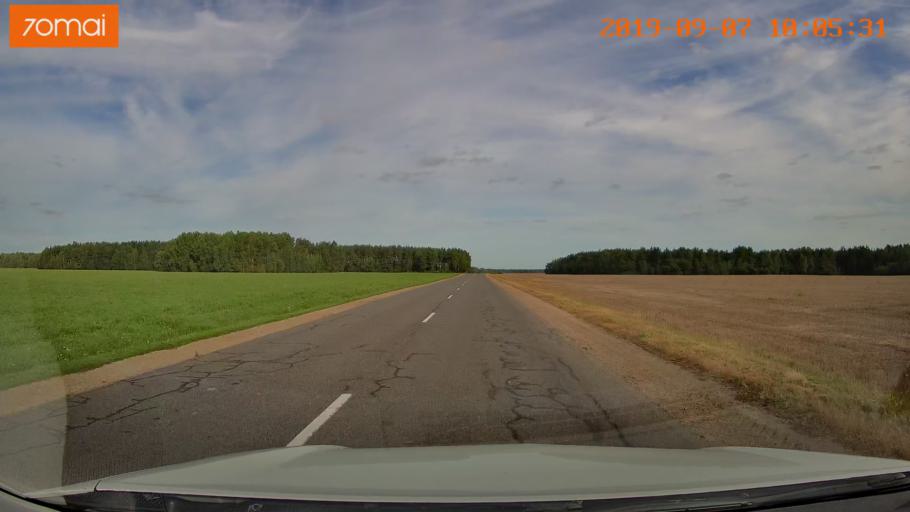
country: BY
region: Grodnenskaya
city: Voranava
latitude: 54.0486
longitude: 25.4070
